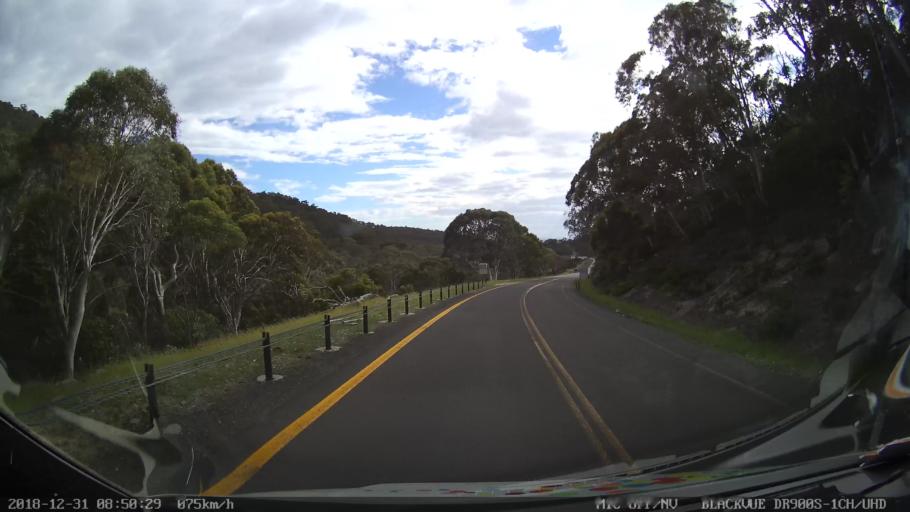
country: AU
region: New South Wales
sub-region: Snowy River
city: Jindabyne
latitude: -36.3525
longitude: 148.5167
